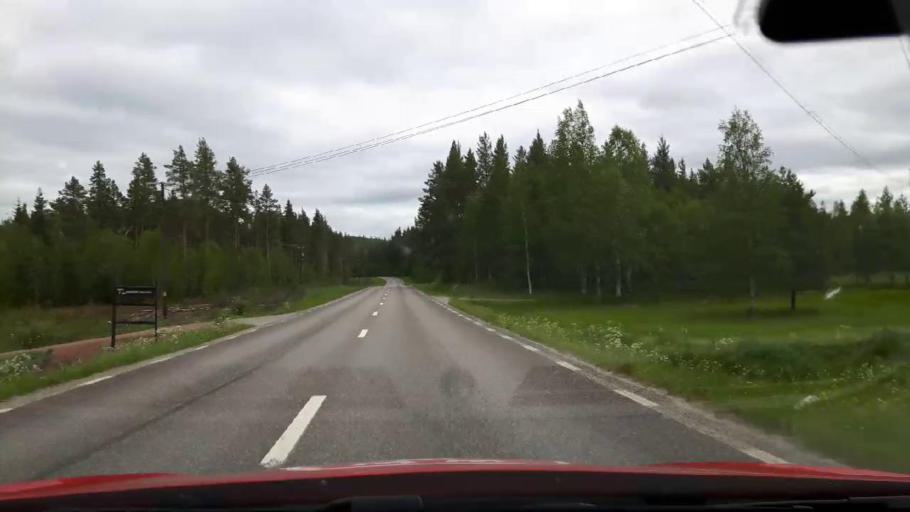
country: SE
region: Jaemtland
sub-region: Ragunda Kommun
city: Hammarstrand
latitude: 63.0669
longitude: 16.3879
